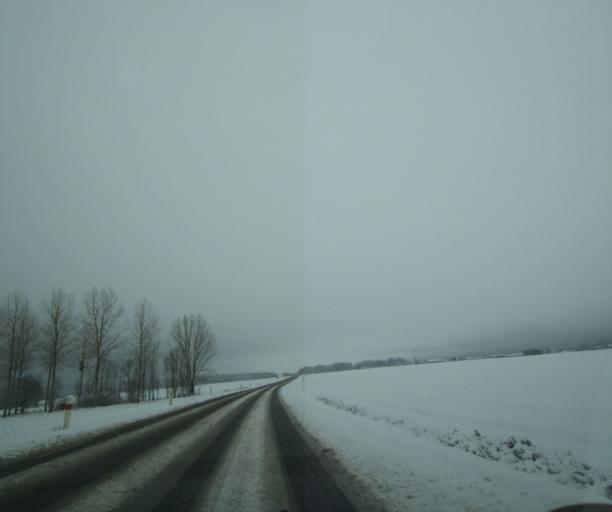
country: FR
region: Champagne-Ardenne
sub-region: Departement de la Haute-Marne
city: Wassy
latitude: 48.5589
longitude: 4.9250
